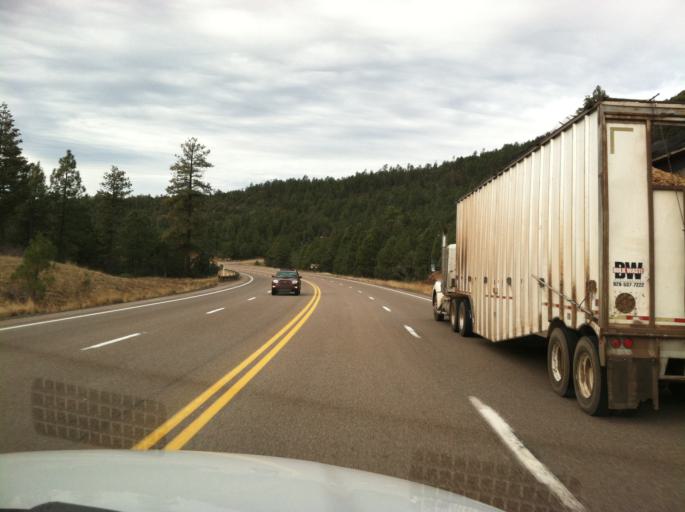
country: US
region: Arizona
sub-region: Gila County
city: Star Valley
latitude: 34.3060
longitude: -110.9470
